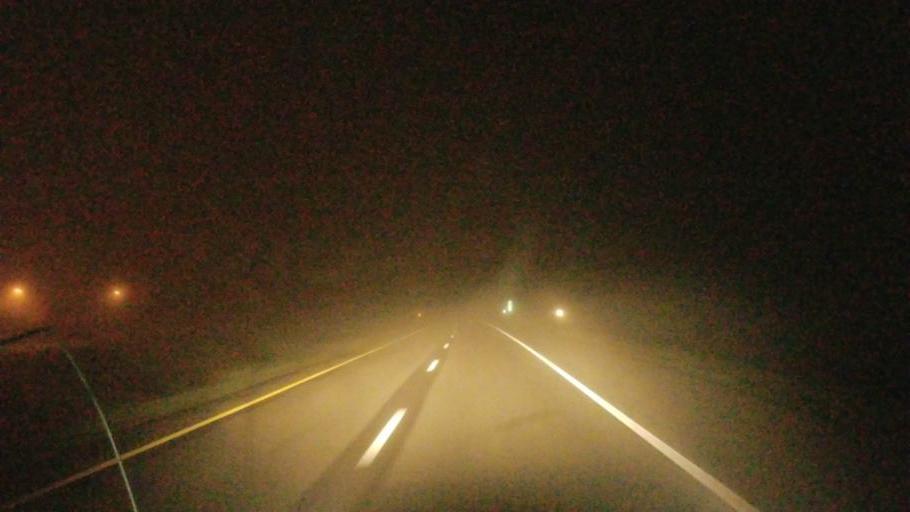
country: US
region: New York
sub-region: Cattaraugus County
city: Allegany
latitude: 42.0952
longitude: -78.5348
